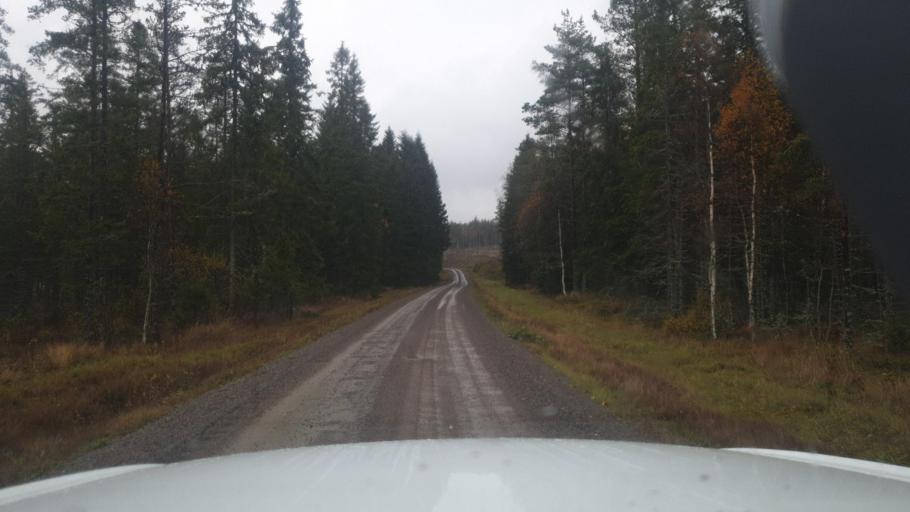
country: SE
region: Vaermland
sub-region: Eda Kommun
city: Charlottenberg
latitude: 60.0475
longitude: 12.6298
